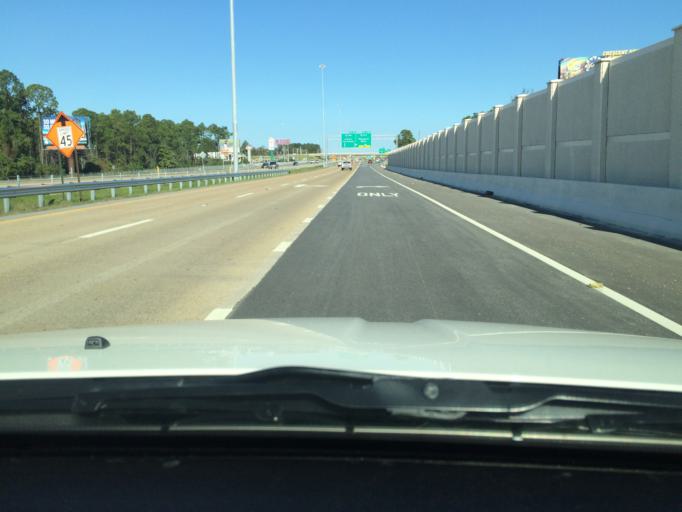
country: US
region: Mississippi
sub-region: Harrison County
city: D'Iberville
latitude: 30.4399
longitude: -88.8948
